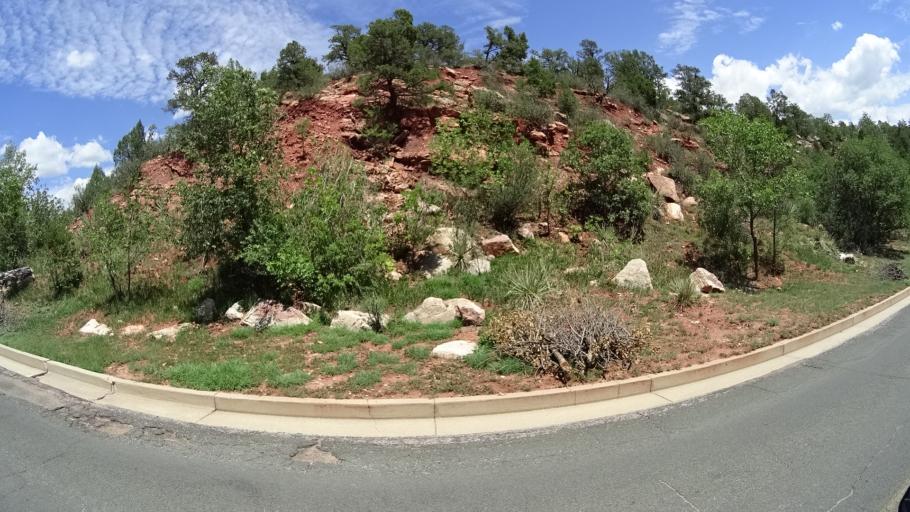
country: US
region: Colorado
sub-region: El Paso County
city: Manitou Springs
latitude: 38.8626
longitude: -104.9016
